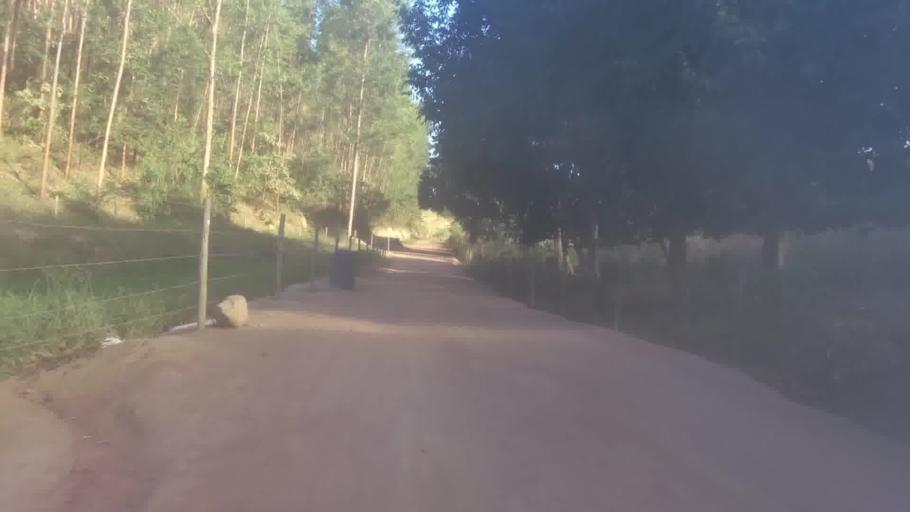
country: BR
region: Espirito Santo
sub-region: Mimoso Do Sul
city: Mimoso do Sul
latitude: -21.0989
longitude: -41.1375
